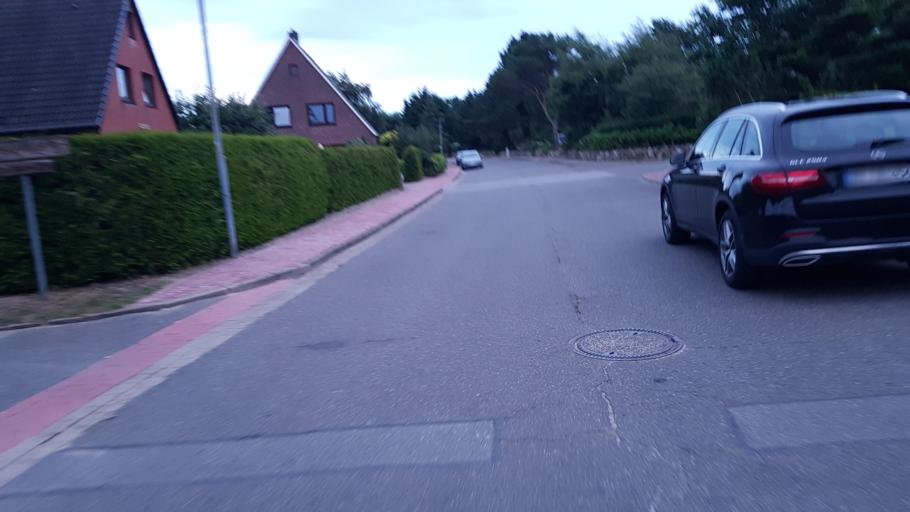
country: DE
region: Schleswig-Holstein
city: Sankt Peter-Ording
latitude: 54.3109
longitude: 8.6240
